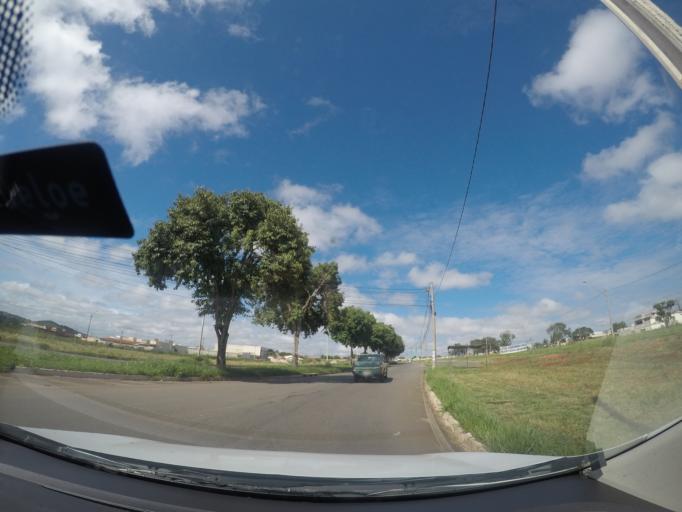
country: BR
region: Goias
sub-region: Goiania
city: Goiania
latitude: -16.6524
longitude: -49.1733
